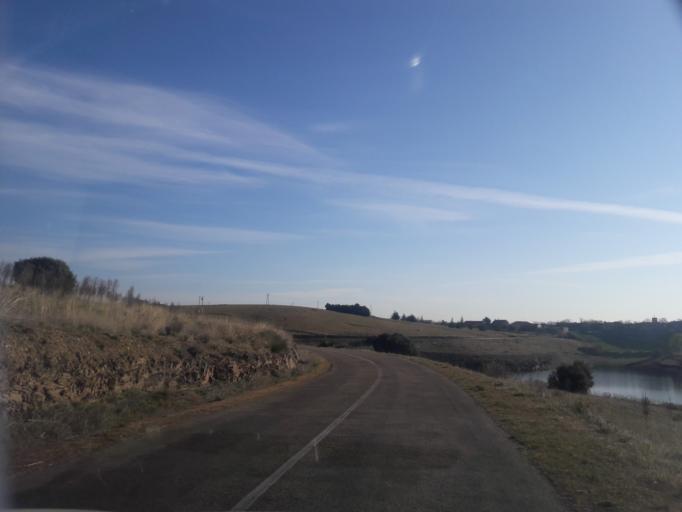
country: ES
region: Castille and Leon
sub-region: Provincia de Salamanca
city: Salvatierra de Tormes
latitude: 40.5867
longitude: -5.6047
